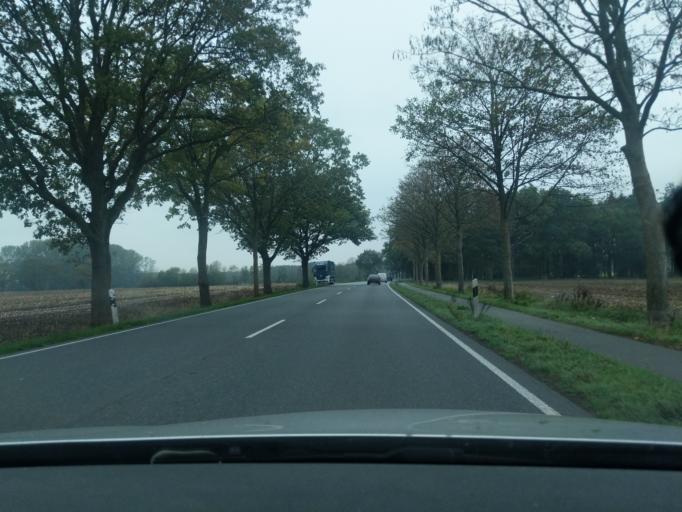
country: DE
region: Lower Saxony
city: Heinbockel
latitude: 53.5949
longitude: 9.3315
